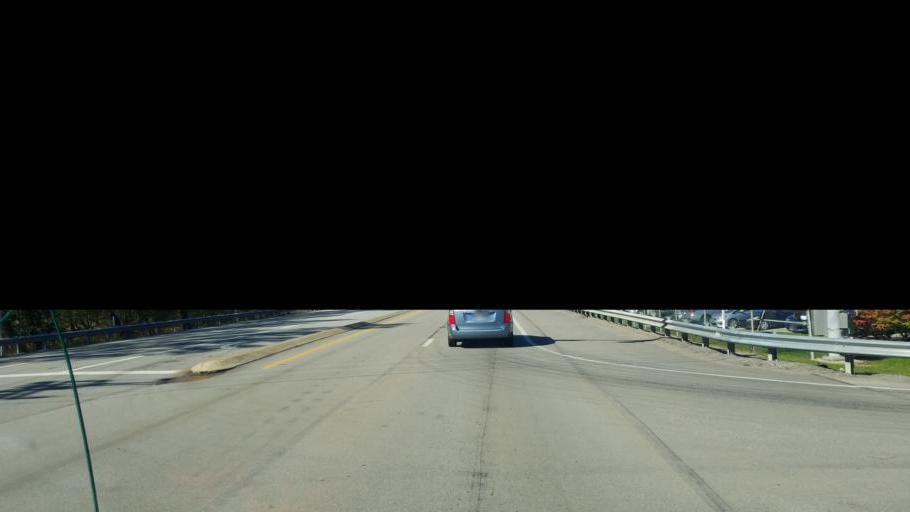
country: US
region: Pennsylvania
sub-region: Westmoreland County
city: Ligonier
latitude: 40.2456
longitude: -79.2447
